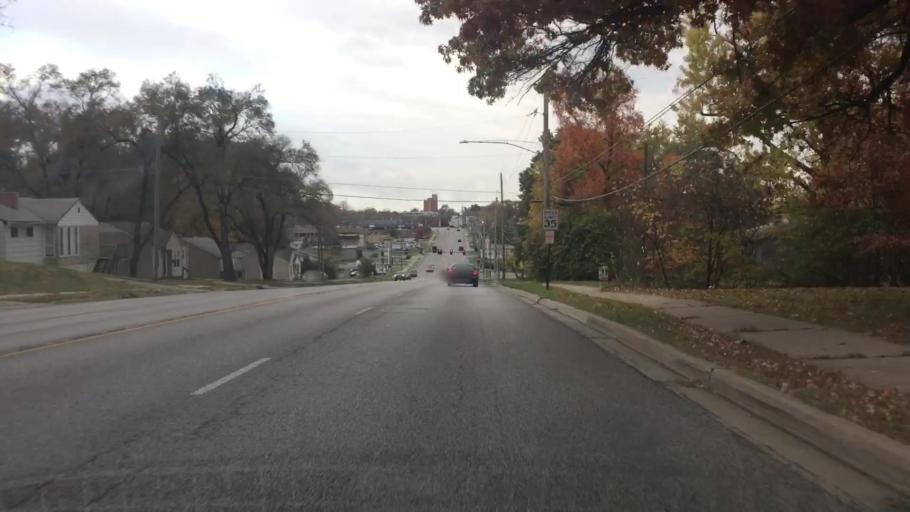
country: US
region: Missouri
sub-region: Jackson County
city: Raytown
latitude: 38.9992
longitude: -94.4638
